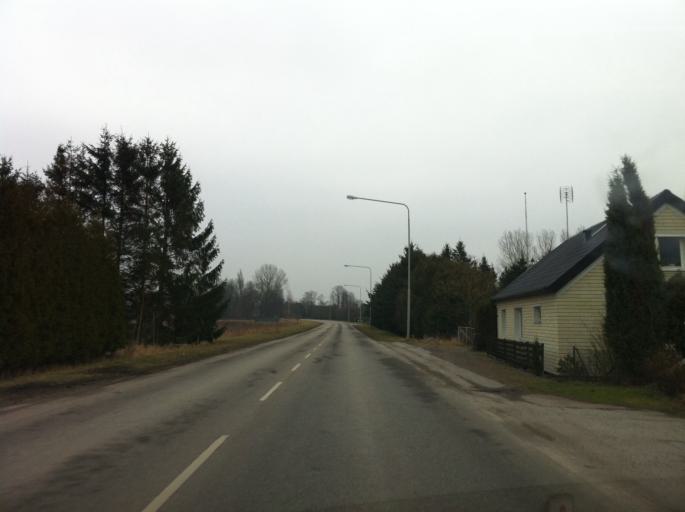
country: SE
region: Skane
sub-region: Landskrona
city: Asmundtorp
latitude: 55.8827
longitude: 12.9152
